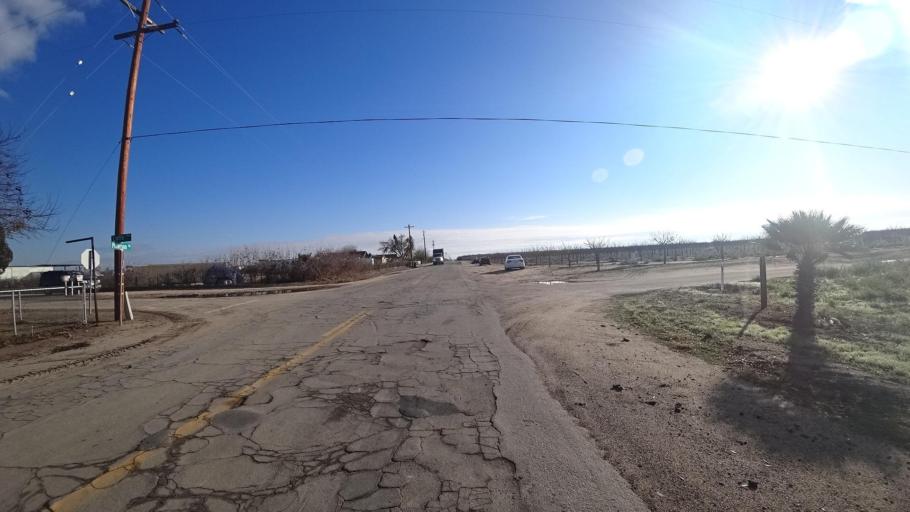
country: US
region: California
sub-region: Kern County
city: McFarland
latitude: 35.7032
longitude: -119.3032
